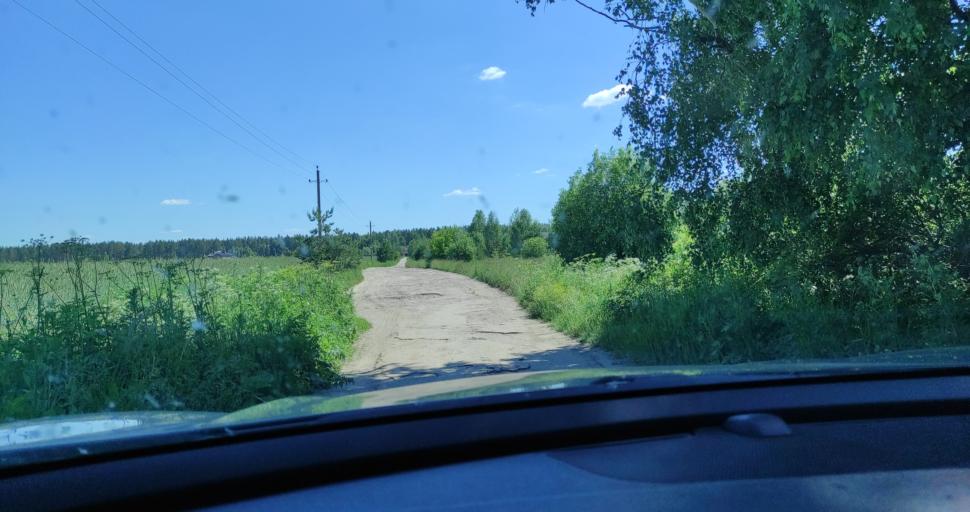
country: RU
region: Rjazan
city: Murmino
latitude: 54.5661
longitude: 40.0963
